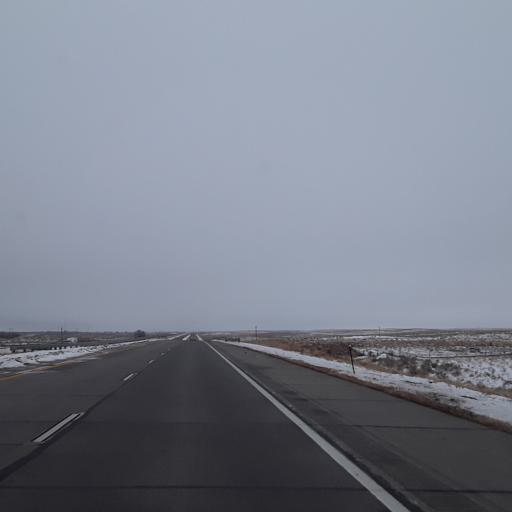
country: US
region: Colorado
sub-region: Logan County
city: Sterling
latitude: 40.5608
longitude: -103.2108
